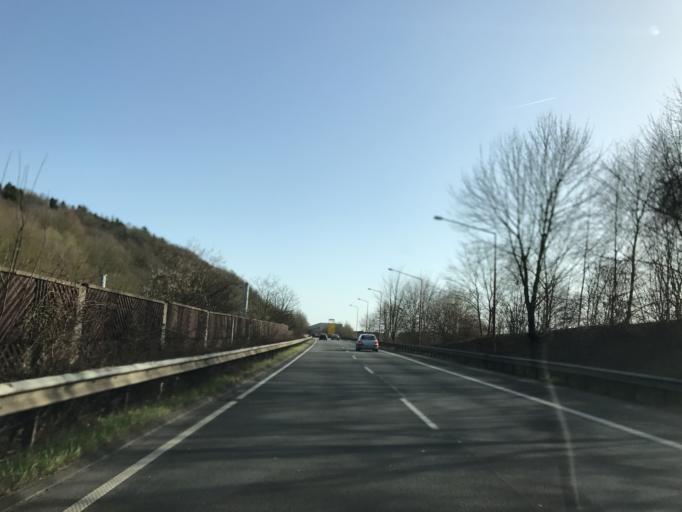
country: DE
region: North Rhine-Westphalia
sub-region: Regierungsbezirk Koln
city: Konigswinter
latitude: 50.6884
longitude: 7.1889
